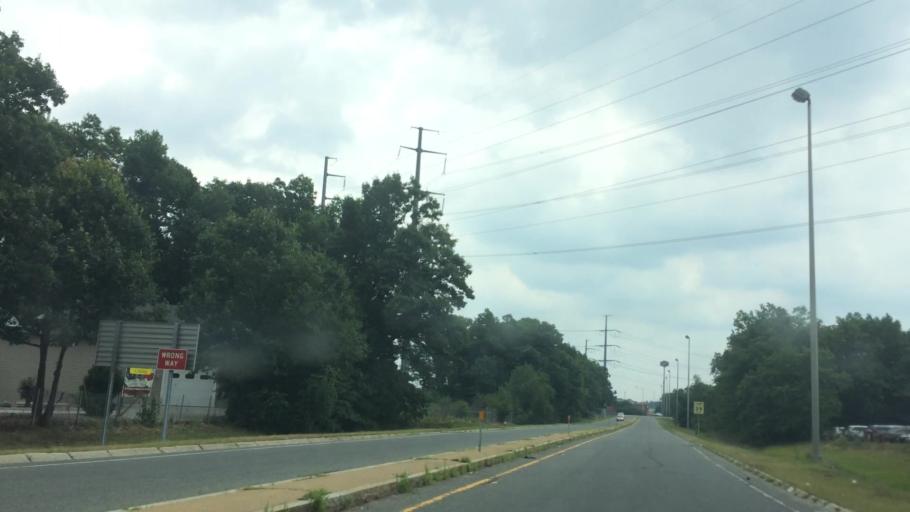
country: US
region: Massachusetts
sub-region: Hampden County
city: North Chicopee
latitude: 42.1728
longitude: -72.5863
